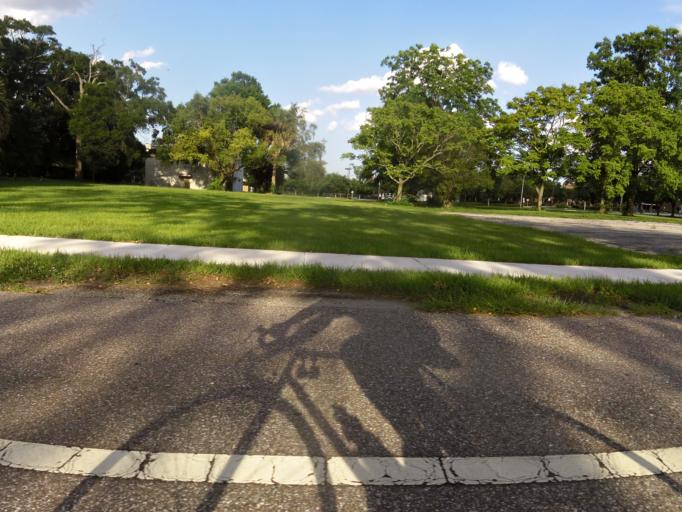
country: US
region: Florida
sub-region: Duval County
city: Jacksonville
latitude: 30.3371
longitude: -81.6639
